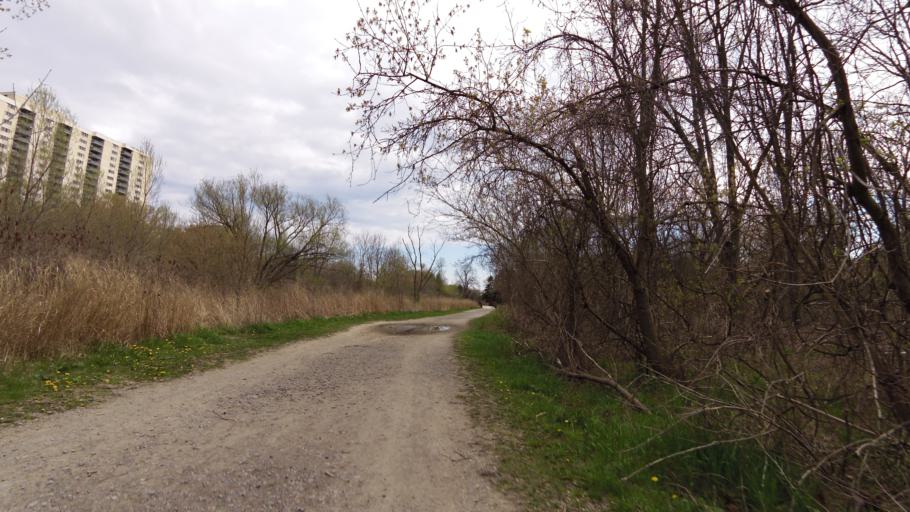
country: CA
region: Ontario
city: Etobicoke
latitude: 43.6406
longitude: -79.5879
